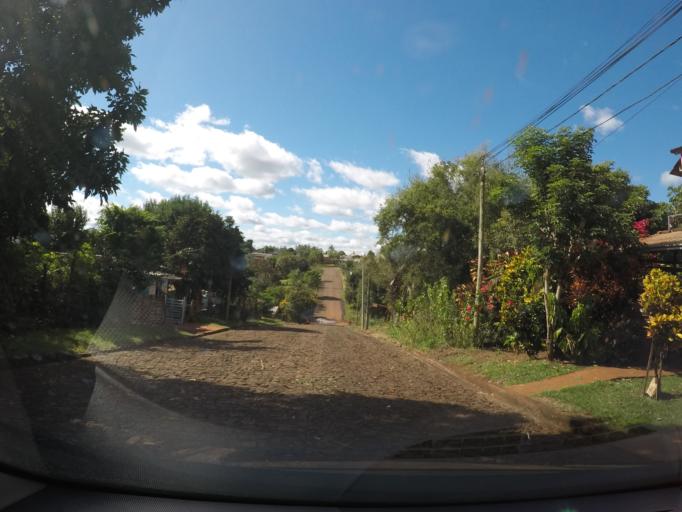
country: AR
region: Misiones
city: Puerto Rico
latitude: -26.7974
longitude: -55.0160
